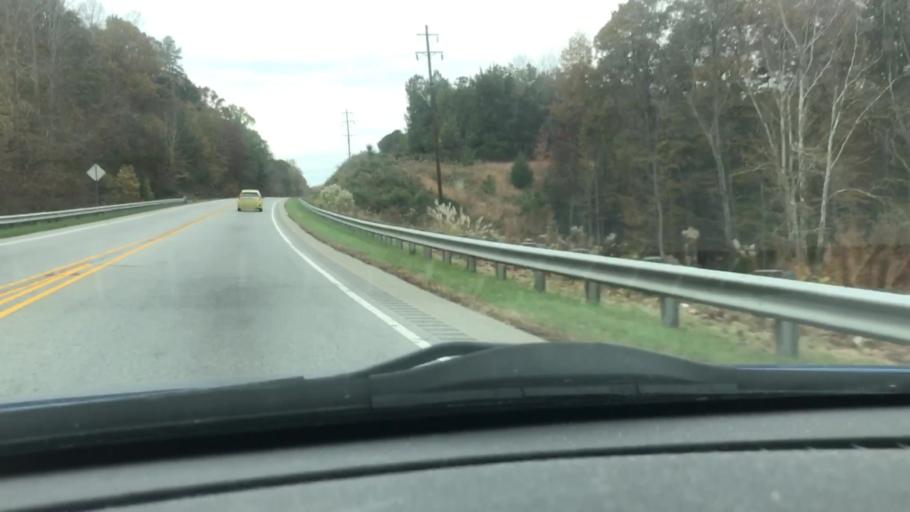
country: US
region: North Carolina
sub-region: Davidson County
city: Thomasville
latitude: 35.7534
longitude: -80.0391
